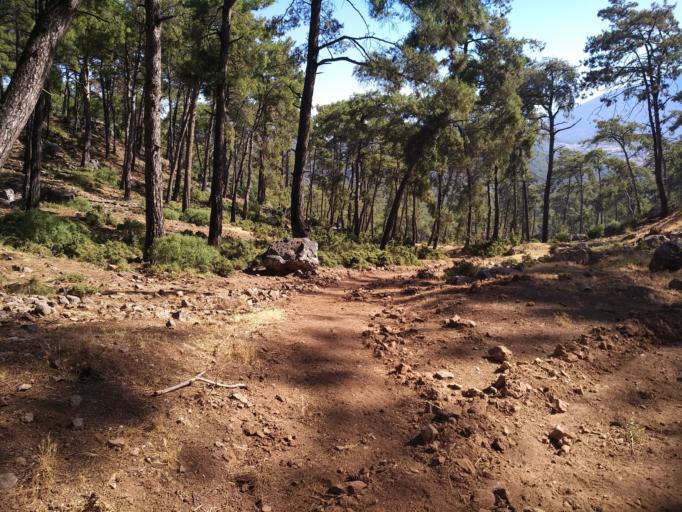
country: TR
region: Mugla
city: OEluedeniz
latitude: 36.5672
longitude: 29.1223
